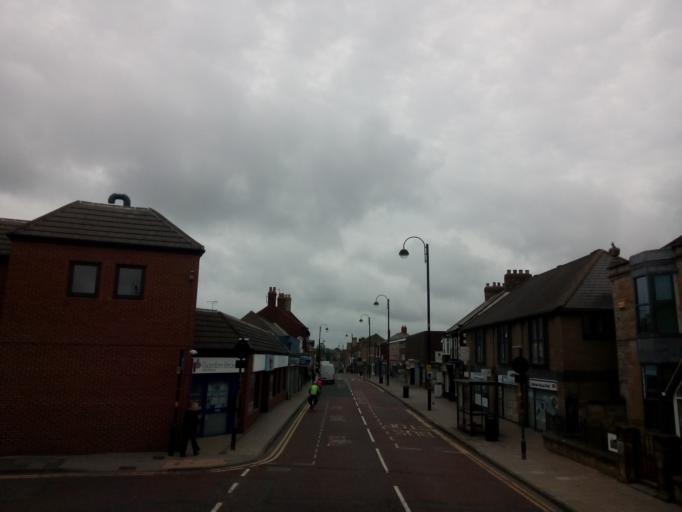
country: GB
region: England
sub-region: County Durham
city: Chester-le-Street
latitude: 54.8531
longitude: -1.5734
